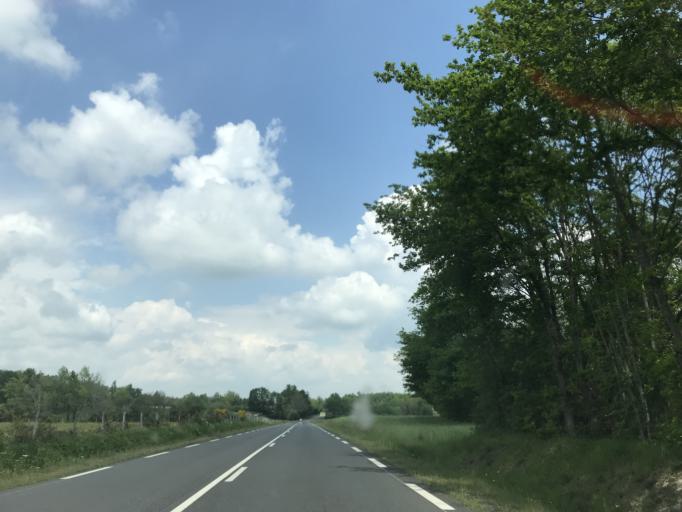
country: FR
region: Auvergne
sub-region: Departement du Puy-de-Dome
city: Peschadoires
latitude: 45.8199
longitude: 3.5060
